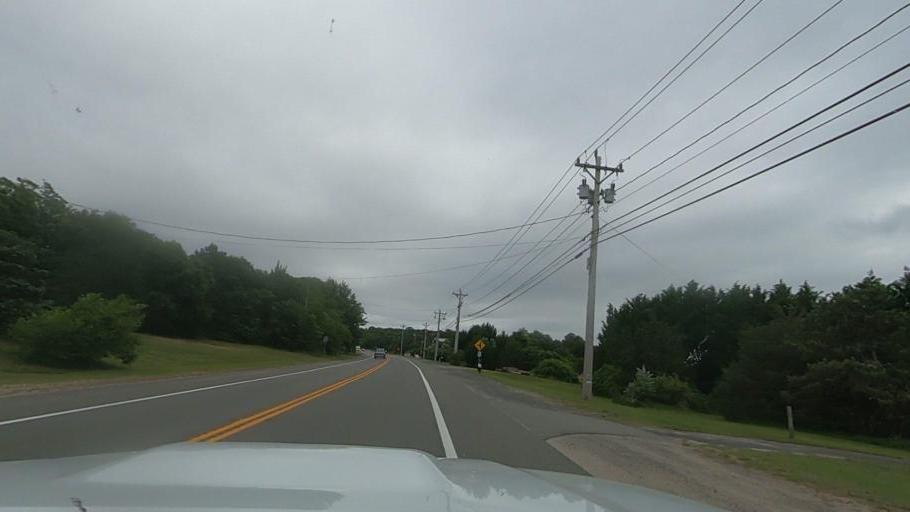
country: US
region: Massachusetts
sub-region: Barnstable County
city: Truro
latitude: 42.0153
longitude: -70.0713
